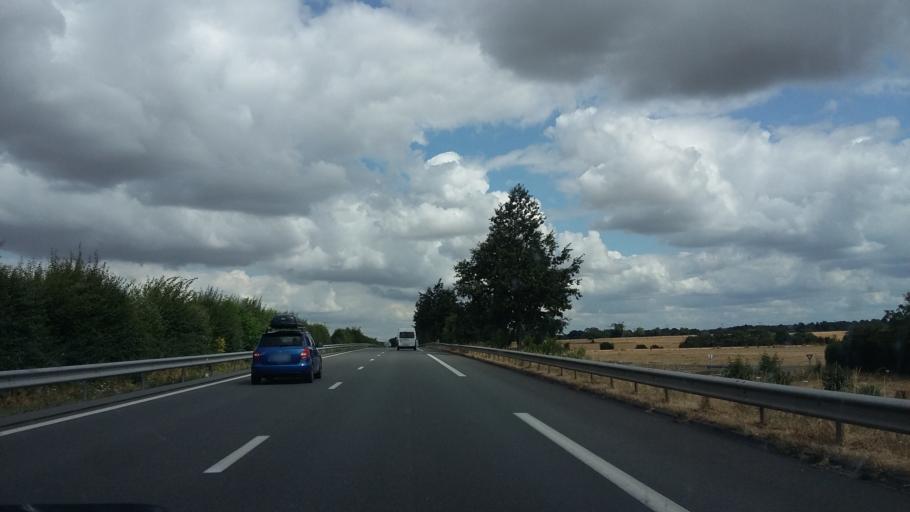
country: FR
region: Poitou-Charentes
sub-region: Departement de la Vienne
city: Couhe
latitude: 46.3392
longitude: 0.1860
